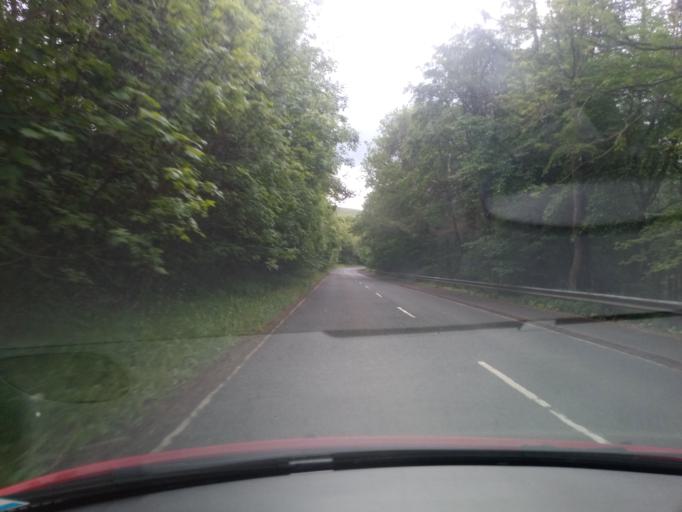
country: GB
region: Scotland
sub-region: The Scottish Borders
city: Galashiels
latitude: 55.6345
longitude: -2.8281
